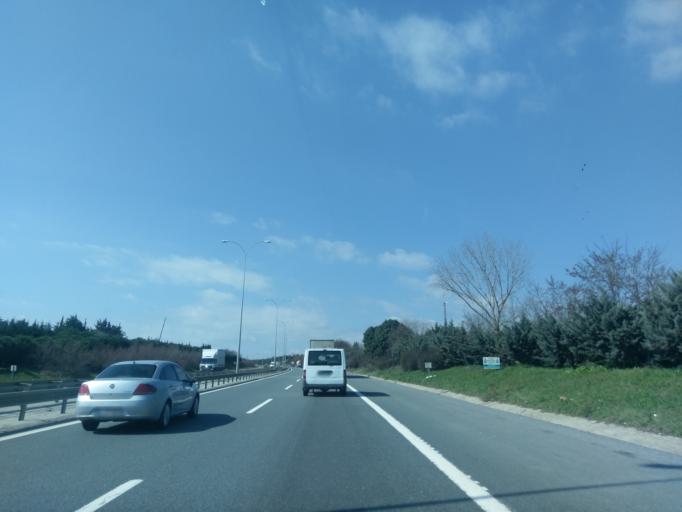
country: TR
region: Istanbul
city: Ortakoy
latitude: 41.0959
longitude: 28.3566
